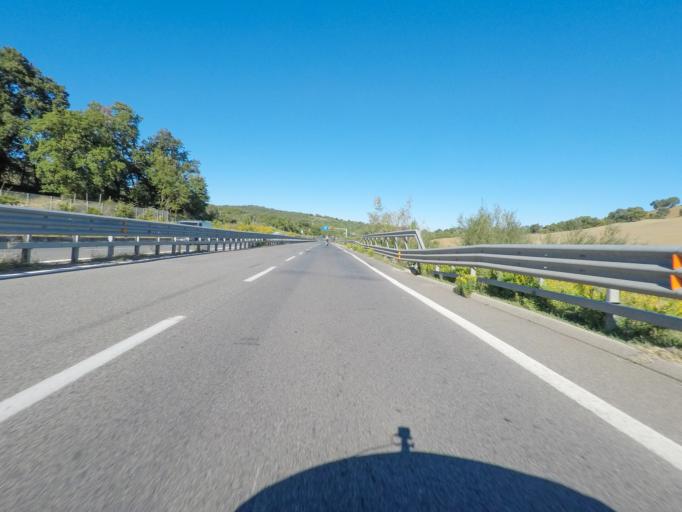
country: IT
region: Tuscany
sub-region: Provincia di Grosseto
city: Campagnatico
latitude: 42.8831
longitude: 11.2198
